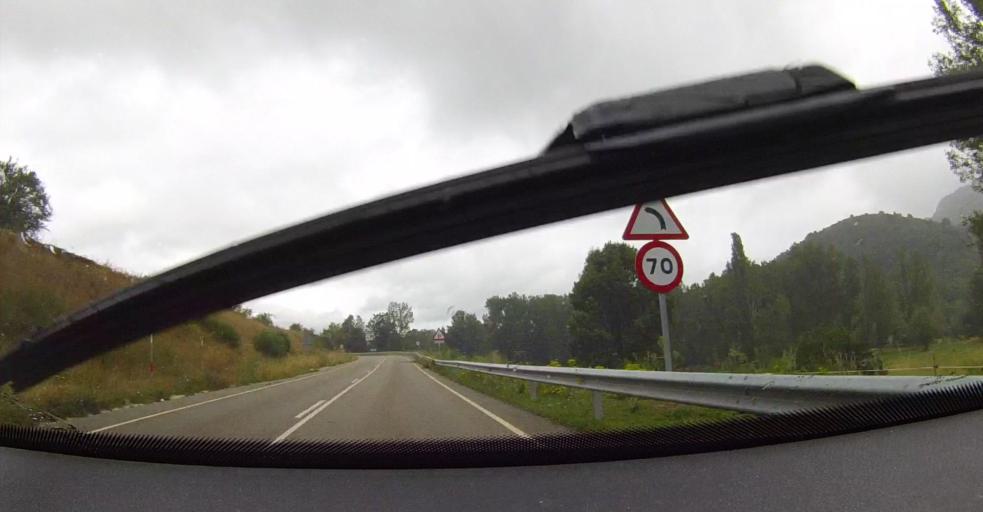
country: ES
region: Castille and Leon
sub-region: Provincia de Leon
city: Acebedo
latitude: 43.0385
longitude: -5.0980
